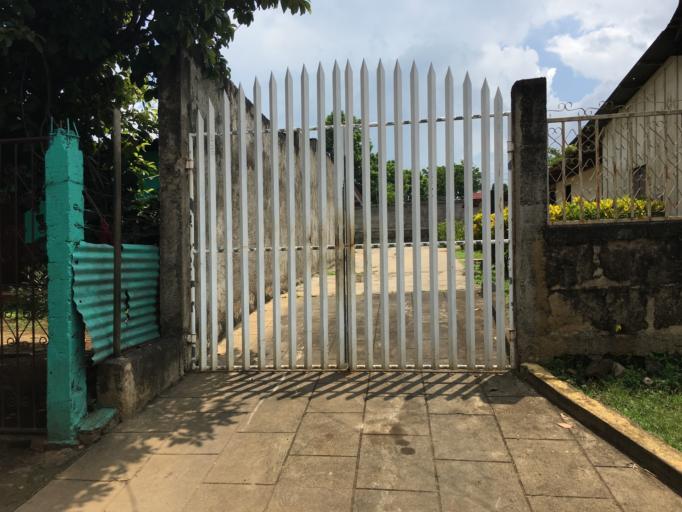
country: NI
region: Masaya
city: Masaya
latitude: 11.9808
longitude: -86.0934
